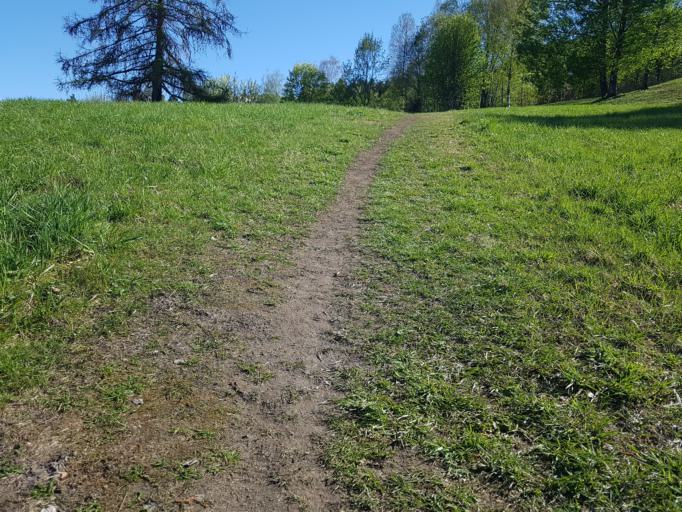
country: NO
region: Buskerud
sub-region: Drammen
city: Drammen
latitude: 59.7275
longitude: 10.2021
